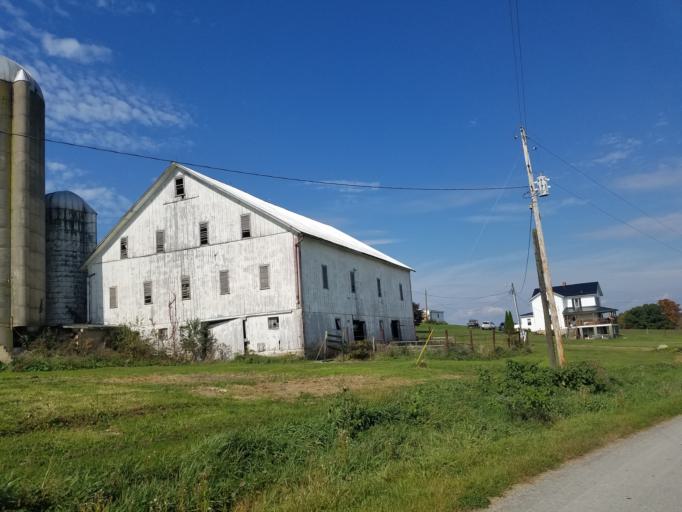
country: US
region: Pennsylvania
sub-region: Clarion County
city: Knox
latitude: 41.2466
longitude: -79.5634
